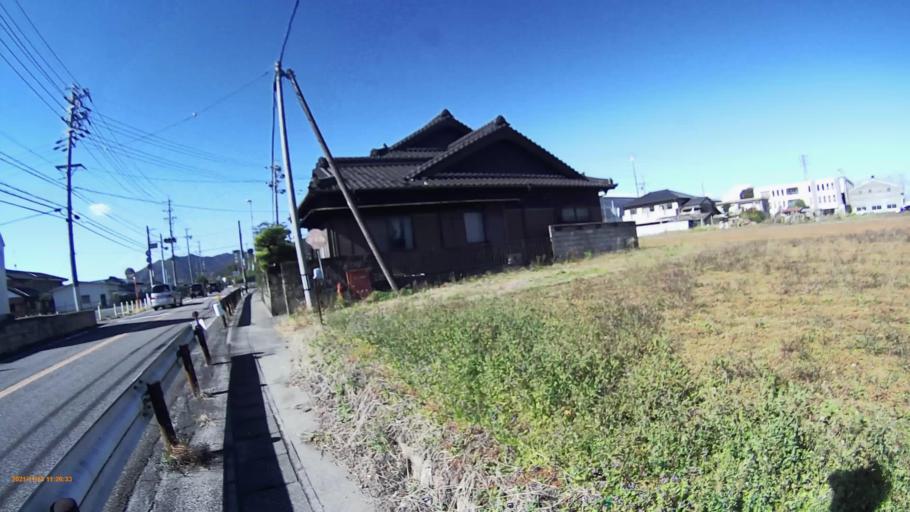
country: JP
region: Gifu
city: Minokamo
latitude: 35.4279
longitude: 136.9950
